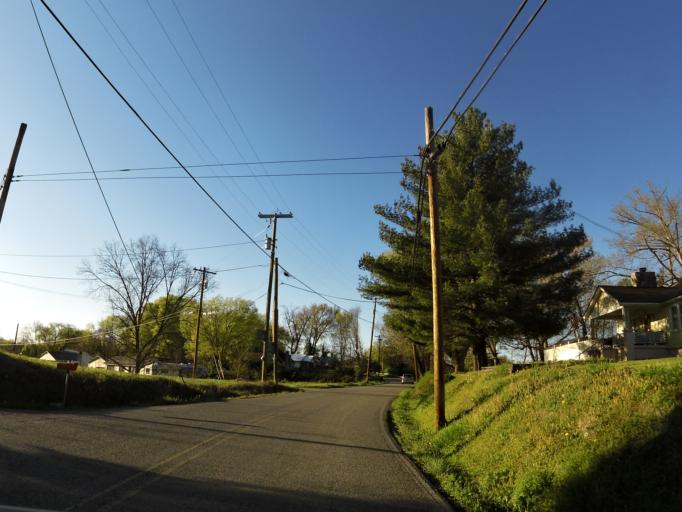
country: US
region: Tennessee
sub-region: Knox County
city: Knoxville
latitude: 35.9747
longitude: -83.8432
